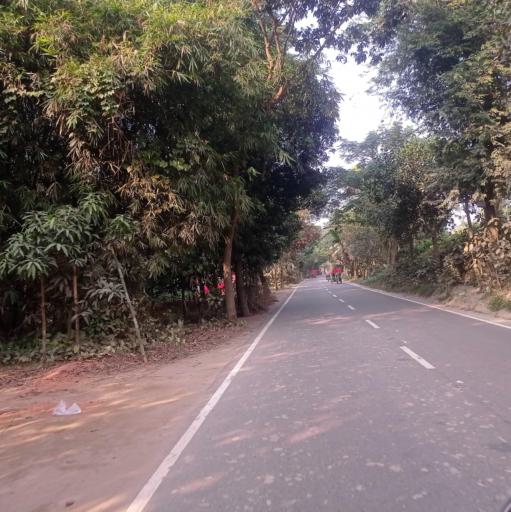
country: BD
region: Dhaka
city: Bhairab Bazar
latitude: 24.0896
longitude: 90.8499
